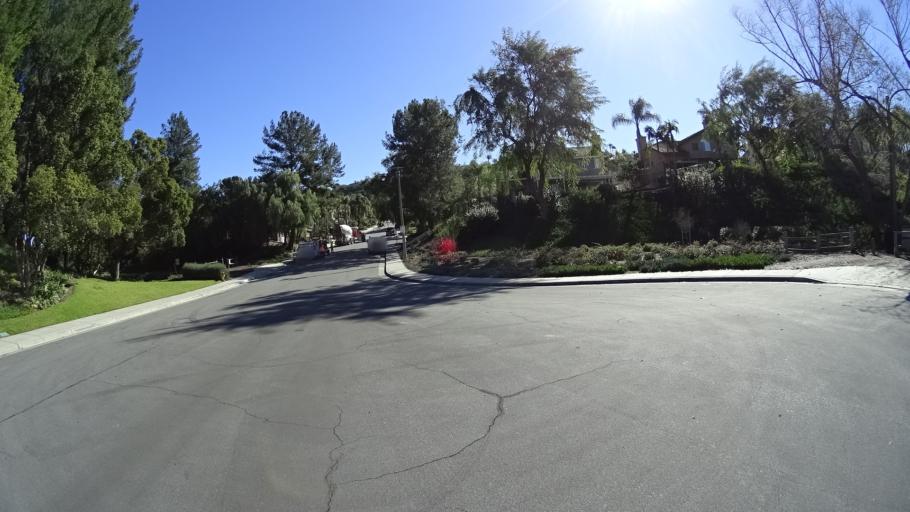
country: US
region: California
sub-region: Orange County
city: Yorba Linda
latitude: 33.8547
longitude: -117.7522
